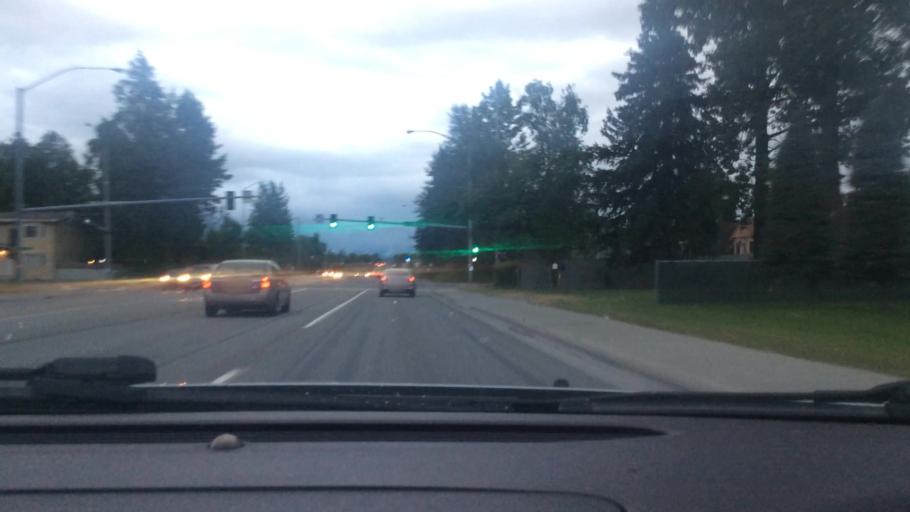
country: US
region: Alaska
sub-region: Anchorage Municipality
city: Anchorage
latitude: 61.1996
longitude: -149.7786
